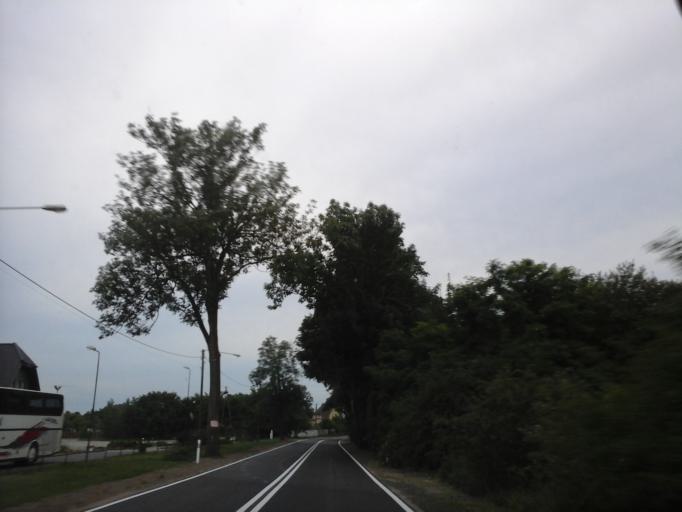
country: PL
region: West Pomeranian Voivodeship
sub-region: Powiat goleniowski
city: Maszewo
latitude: 53.4860
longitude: 15.0634
